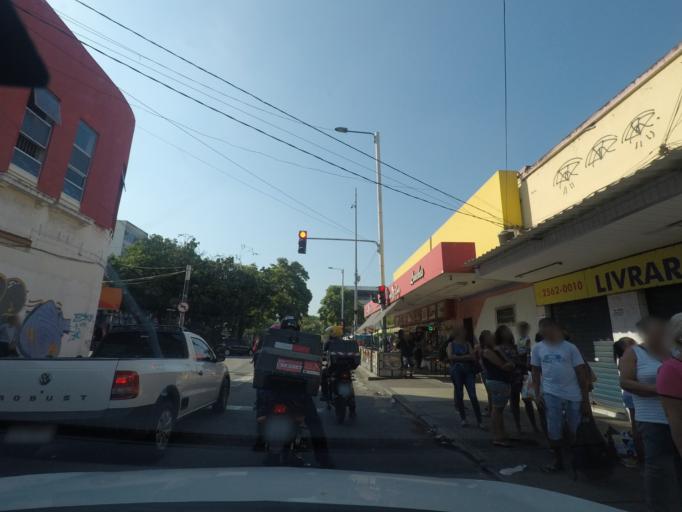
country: BR
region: Rio de Janeiro
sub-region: Rio De Janeiro
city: Rio de Janeiro
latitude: -22.8658
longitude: -43.2557
